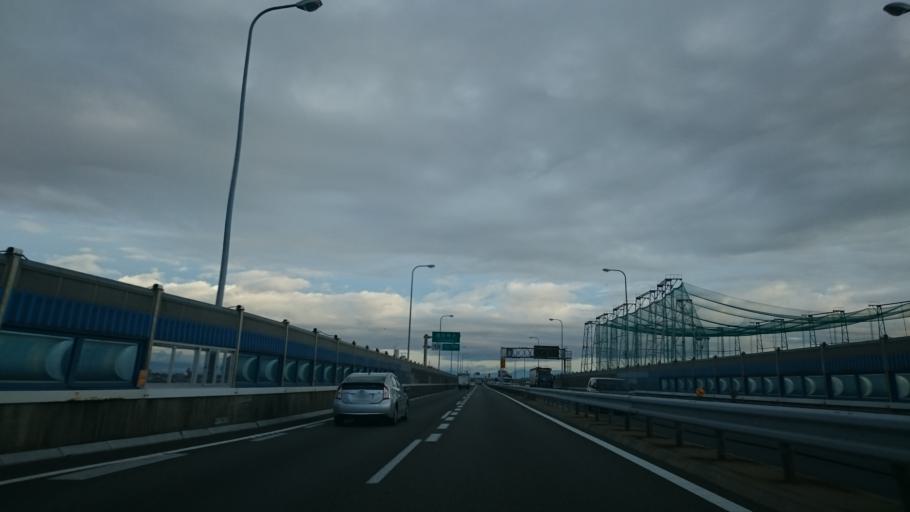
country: JP
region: Aichi
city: Kanie
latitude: 35.1904
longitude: 136.8164
